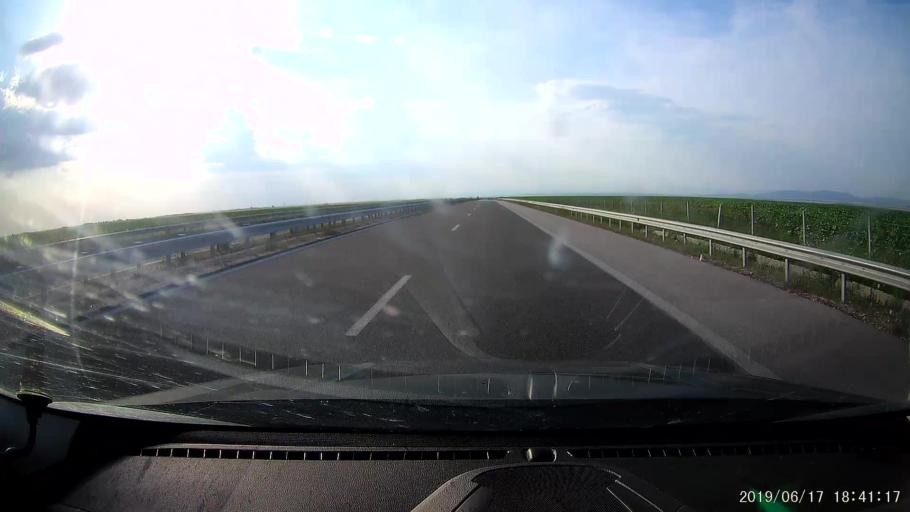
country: BG
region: Stara Zagora
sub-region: Obshtina Chirpan
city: Chirpan
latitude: 42.1696
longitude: 25.2584
